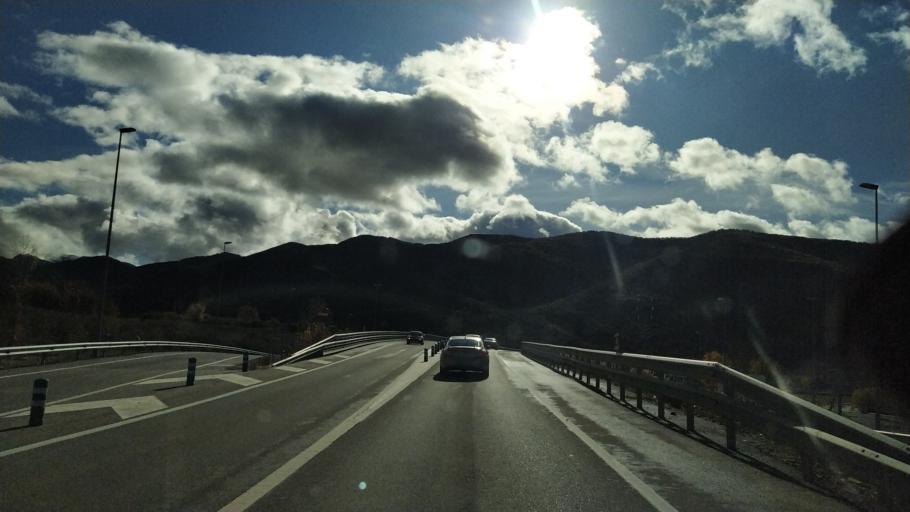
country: ES
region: Aragon
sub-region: Provincia de Huesca
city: Sabinanigo
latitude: 42.5060
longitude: -0.3535
